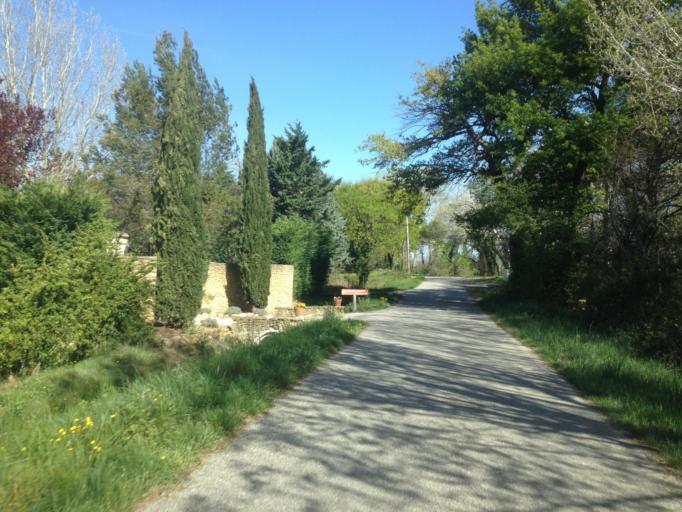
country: FR
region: Provence-Alpes-Cote d'Azur
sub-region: Departement du Vaucluse
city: Caderousse
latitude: 44.1326
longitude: 4.7529
